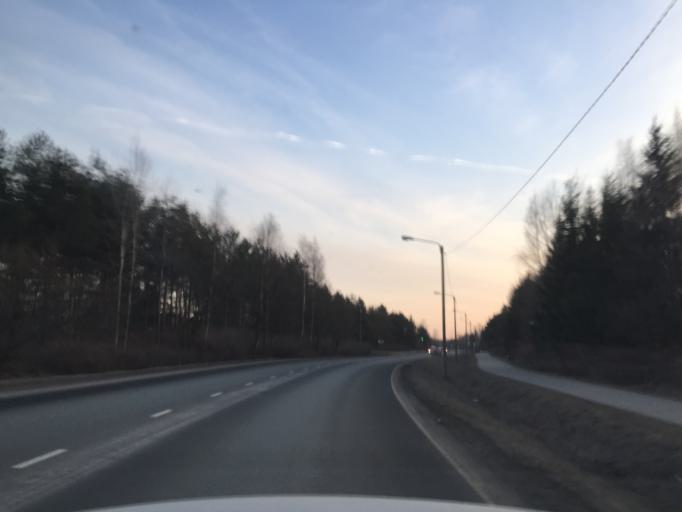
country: FI
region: Uusimaa
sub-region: Helsinki
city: Vantaa
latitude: 60.2626
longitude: 24.9919
